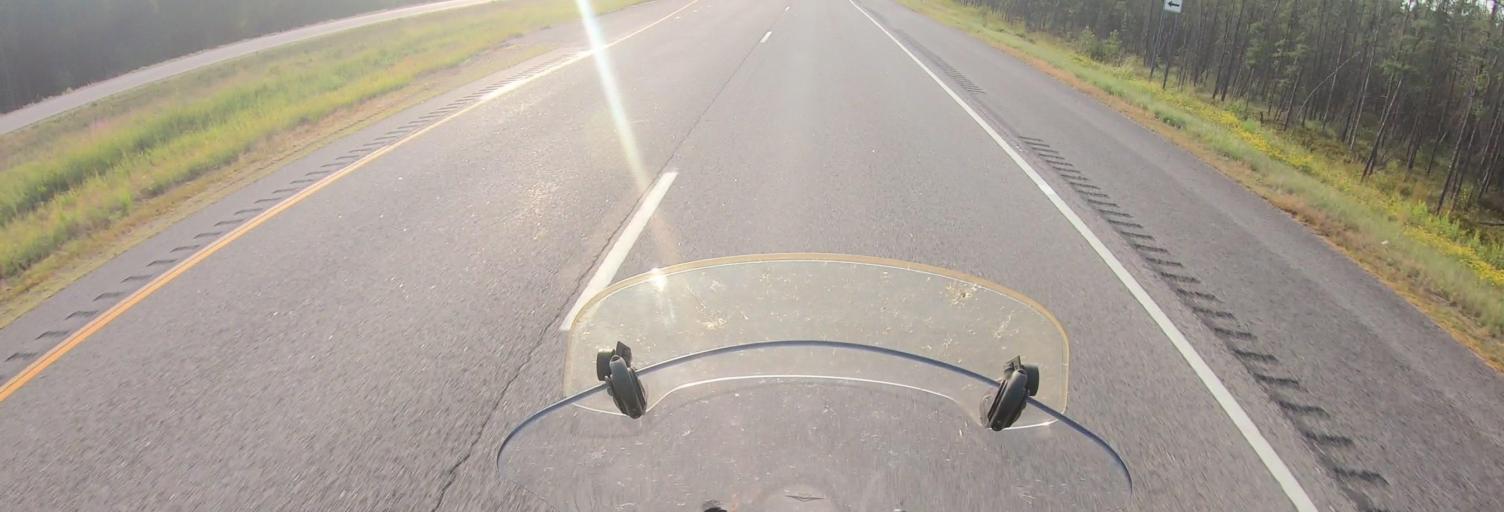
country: US
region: Minnesota
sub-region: Saint Louis County
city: Mountain Iron
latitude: 47.6656
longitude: -92.6284
